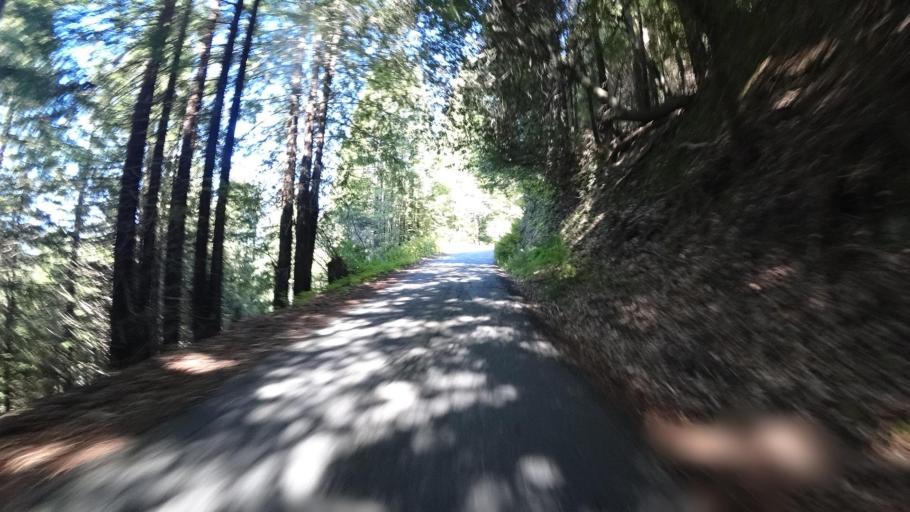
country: US
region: California
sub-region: Humboldt County
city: Rio Dell
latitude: 40.4555
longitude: -123.9929
